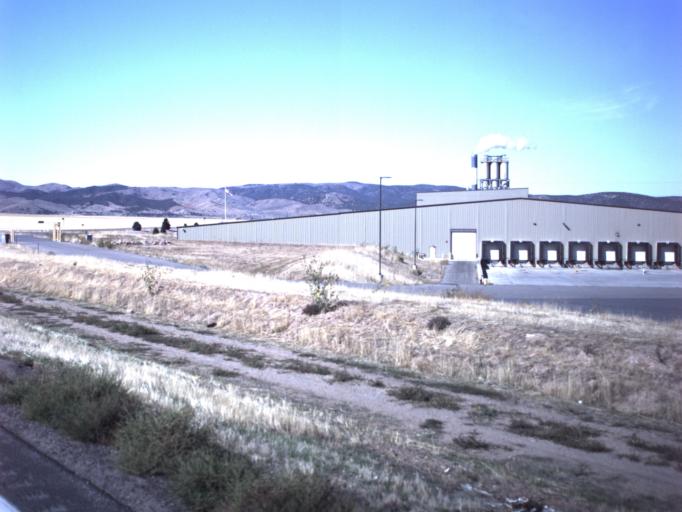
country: US
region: Utah
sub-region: Juab County
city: Nephi
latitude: 39.6690
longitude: -111.8497
